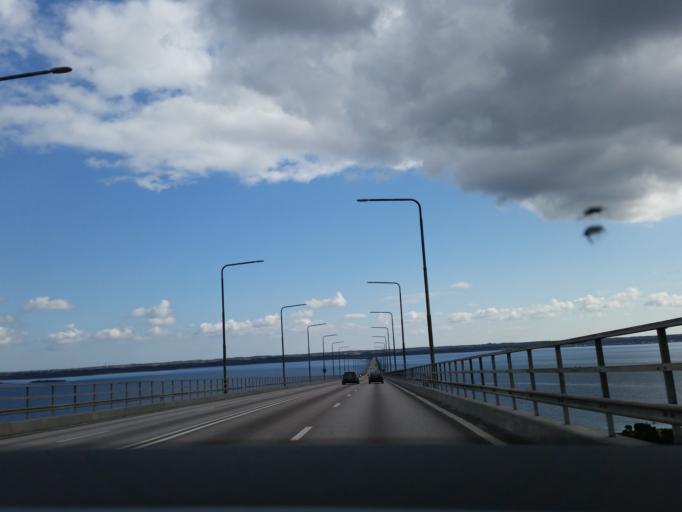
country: SE
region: Kalmar
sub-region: Kalmar Kommun
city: Kalmar
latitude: 56.6777
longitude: 16.4018
